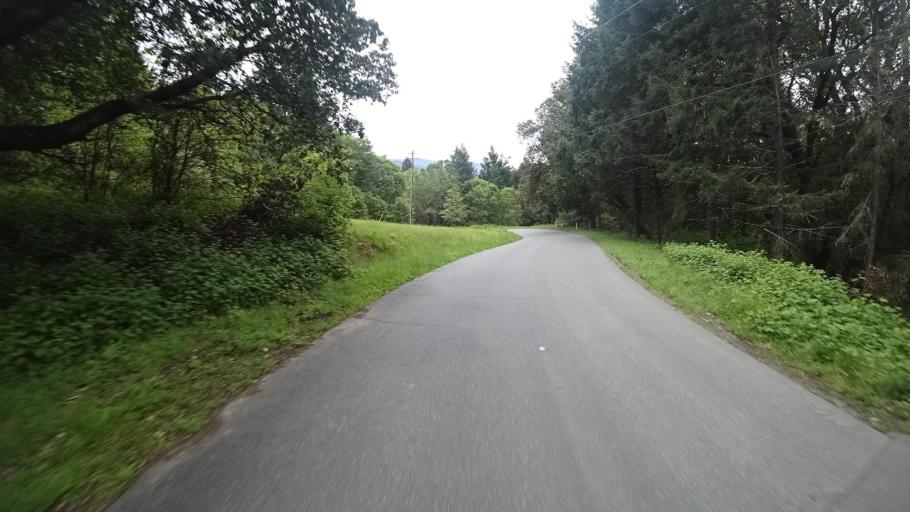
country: US
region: California
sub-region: Humboldt County
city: Willow Creek
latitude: 41.1112
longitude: -123.7124
